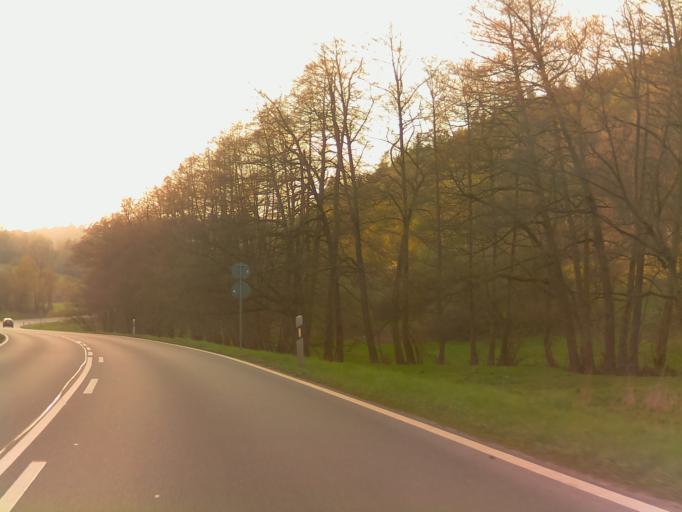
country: DE
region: Thuringia
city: Unterbreizbach
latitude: 50.8594
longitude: 9.9439
